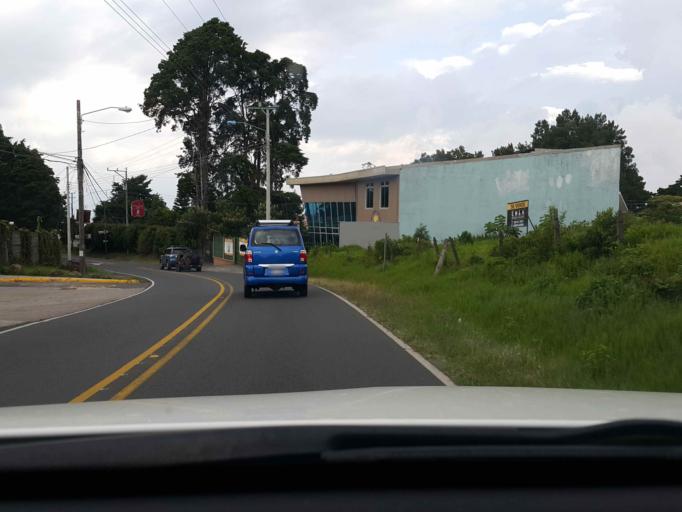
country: CR
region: Heredia
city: San Josecito
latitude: 10.0411
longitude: -84.0899
